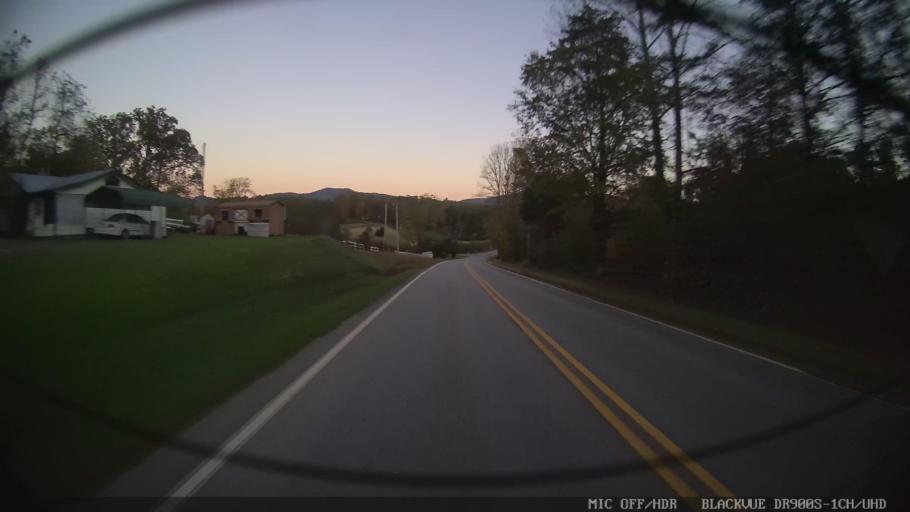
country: US
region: North Carolina
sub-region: Clay County
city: Hayesville
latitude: 34.9691
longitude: -83.8775
